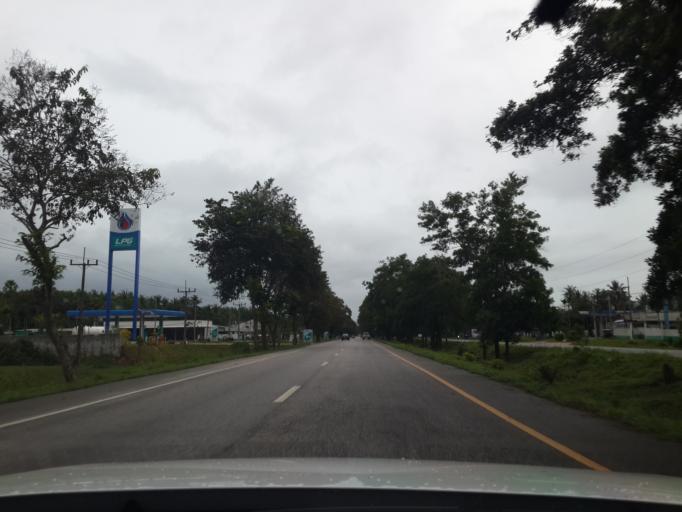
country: TH
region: Songkhla
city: Na Mom
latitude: 6.9583
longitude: 100.5632
